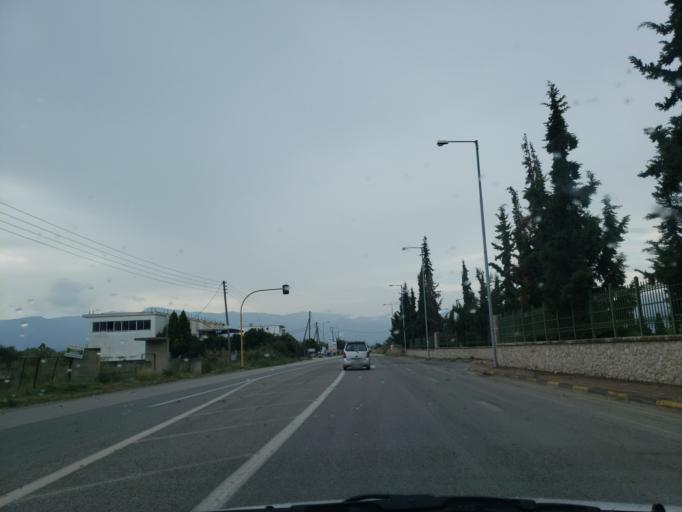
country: GR
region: Central Greece
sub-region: Nomos Fthiotidos
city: Lamia
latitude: 38.8740
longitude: 22.4394
